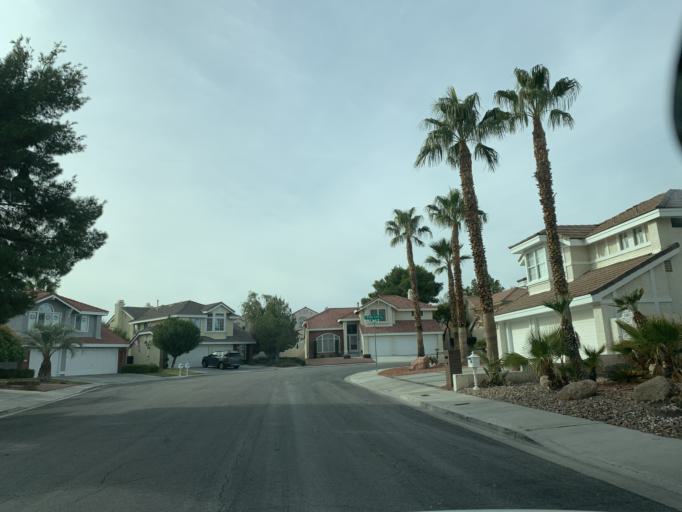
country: US
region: Nevada
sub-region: Clark County
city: Summerlin South
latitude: 36.1367
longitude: -115.3073
